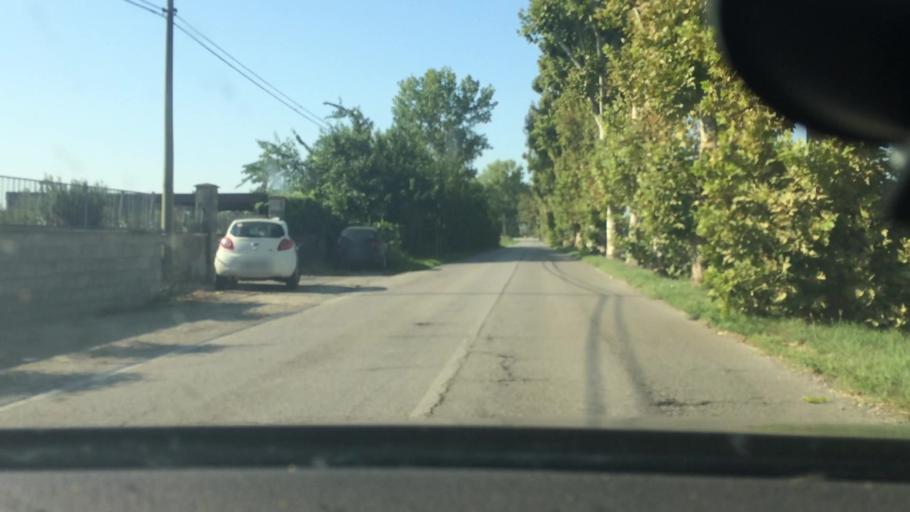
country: IT
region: Emilia-Romagna
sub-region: Provincia di Ferrara
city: Lagosanto
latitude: 44.7509
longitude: 12.1369
